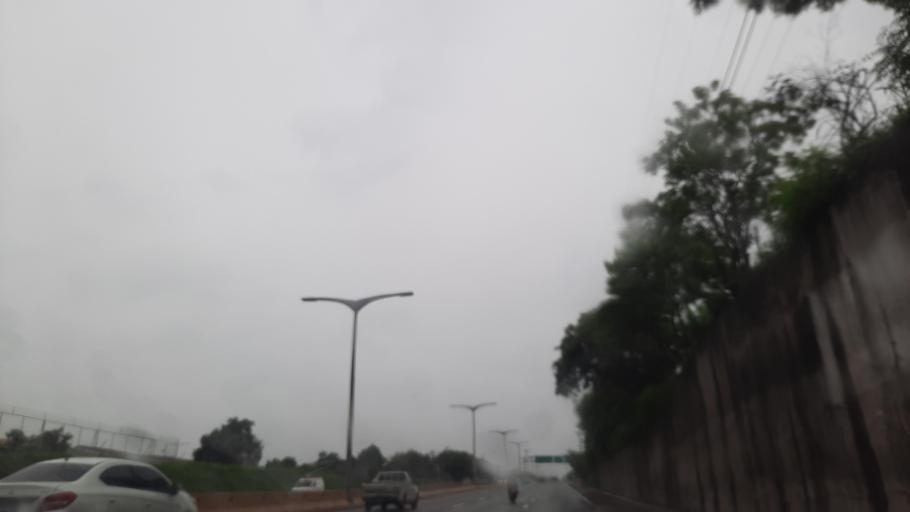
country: SV
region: La Libertad
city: Santa Tecla
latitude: 13.6847
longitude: -89.2767
